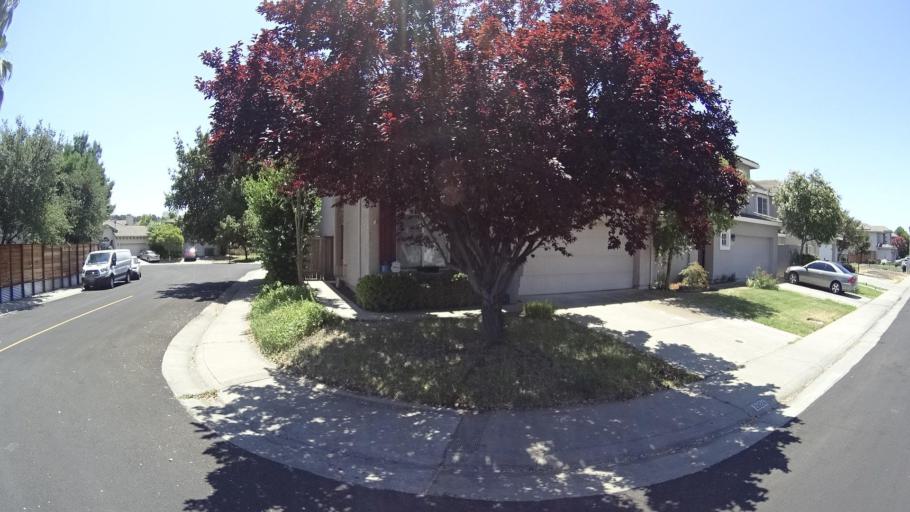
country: US
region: California
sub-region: Placer County
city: Rocklin
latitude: 38.8155
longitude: -121.2609
